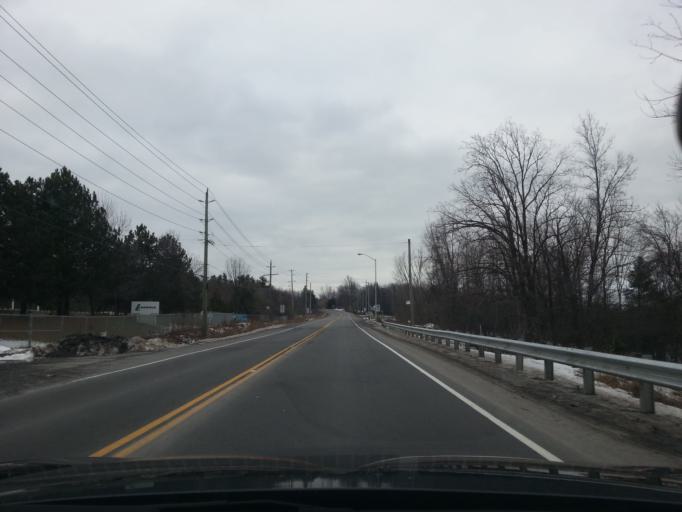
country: CA
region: Ontario
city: Ottawa
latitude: 45.4453
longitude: -75.5767
